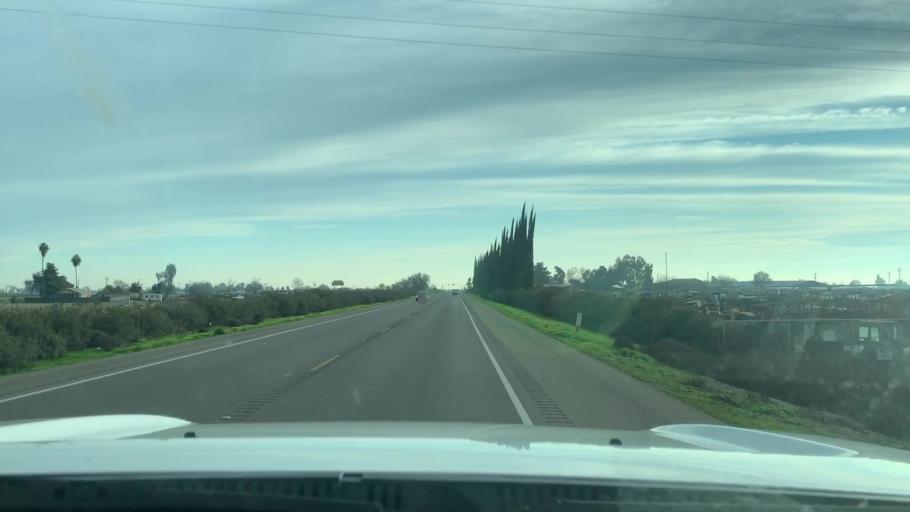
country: US
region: California
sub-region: Fresno County
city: Riverdale
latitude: 36.4384
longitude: -119.7997
